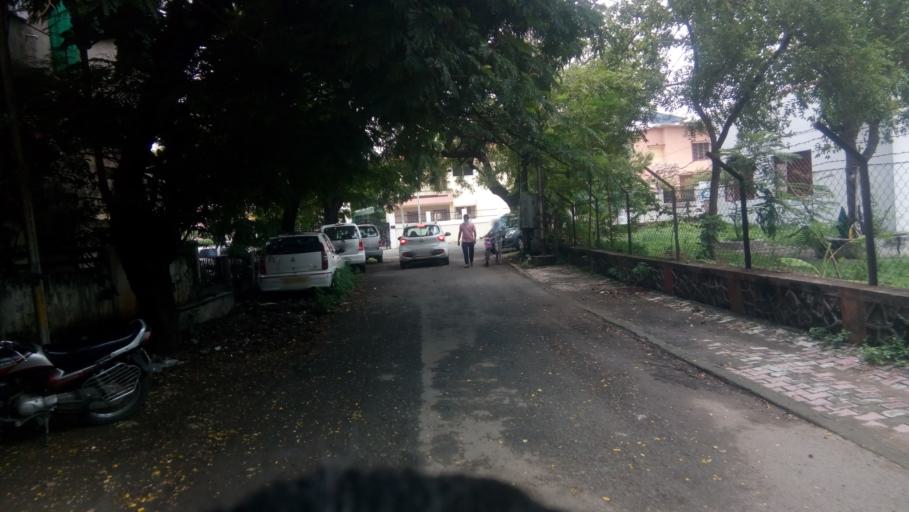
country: IN
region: Maharashtra
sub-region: Nagpur Division
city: Nagpur
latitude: 21.1078
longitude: 79.0640
